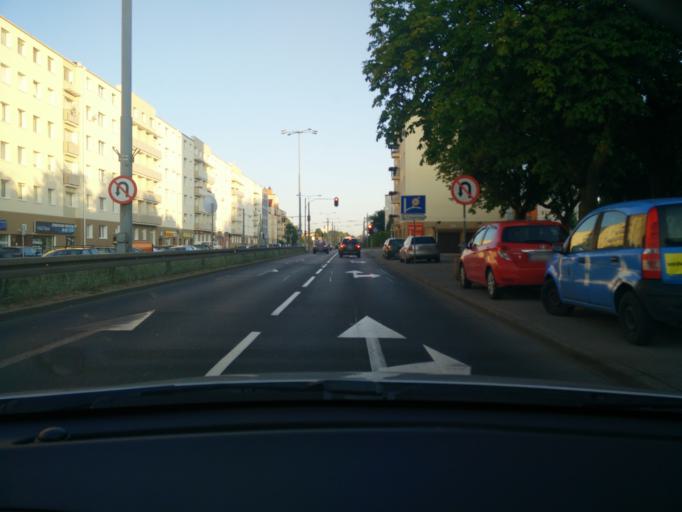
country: PL
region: Pomeranian Voivodeship
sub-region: Gdynia
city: Gdynia
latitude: 54.5128
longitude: 18.5332
